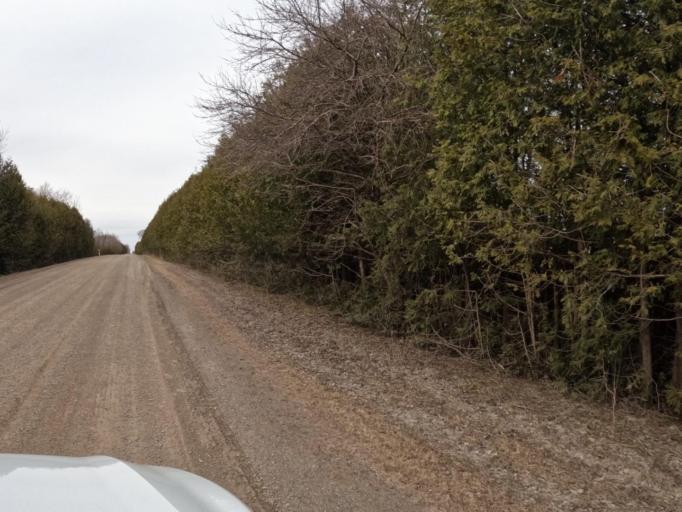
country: CA
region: Ontario
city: Orangeville
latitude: 43.9255
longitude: -80.2566
